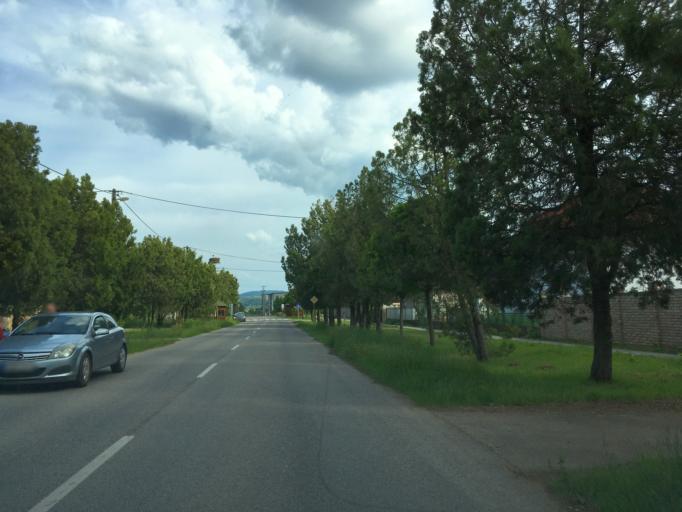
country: HU
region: Komarom-Esztergom
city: Dunaalmas
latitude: 47.7526
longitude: 18.3237
